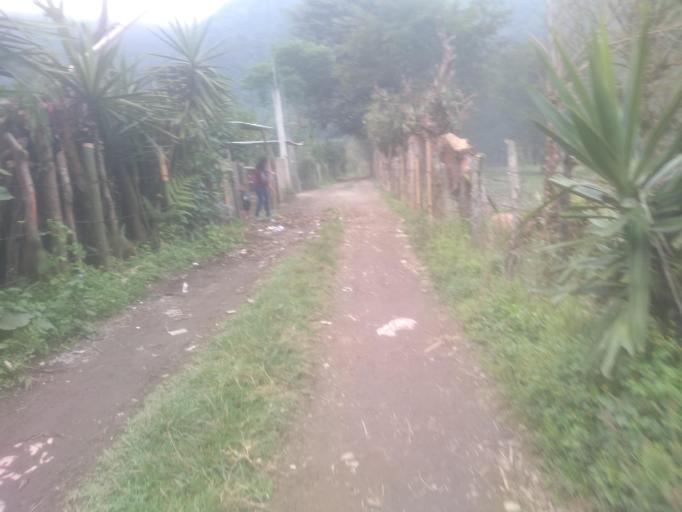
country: MX
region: Veracruz
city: Chocaman
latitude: 19.0007
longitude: -97.0420
